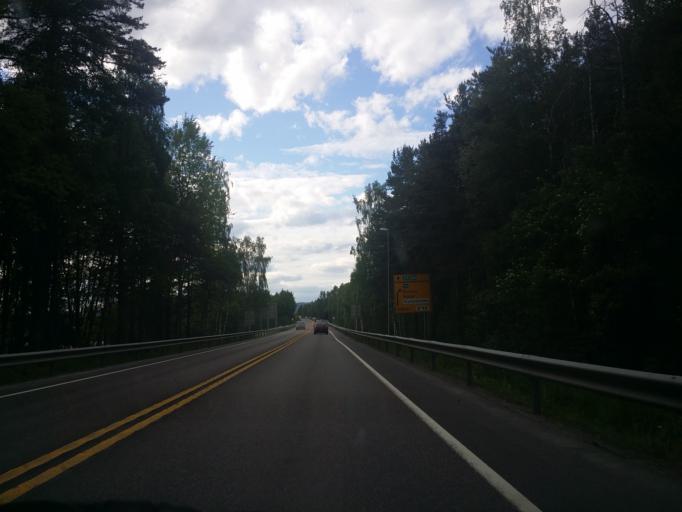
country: NO
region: Hedmark
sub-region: Hamar
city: Hamar
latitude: 60.7924
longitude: 11.1236
